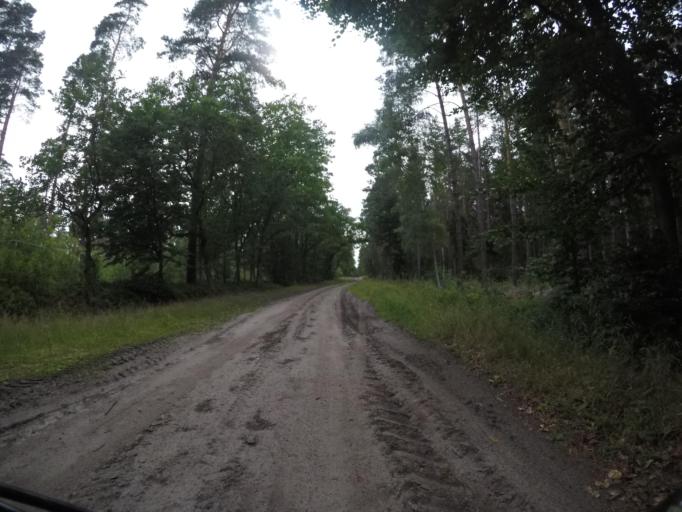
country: DE
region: Mecklenburg-Vorpommern
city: Lubtheen
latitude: 53.2571
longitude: 11.0049
